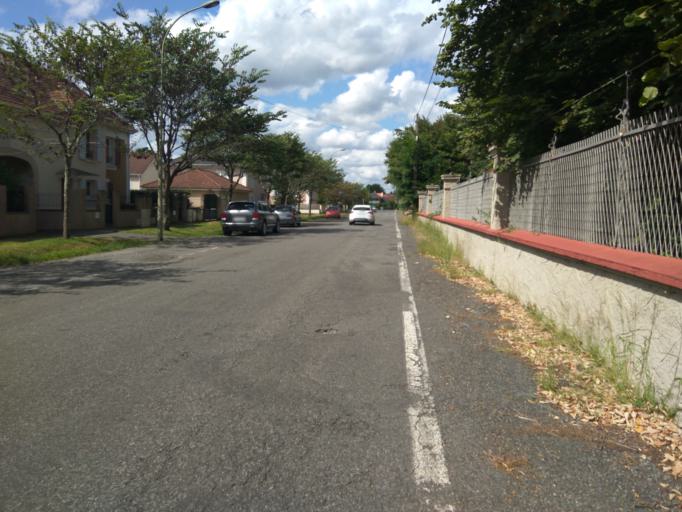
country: FR
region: Aquitaine
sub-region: Departement des Pyrenees-Atlantiques
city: Bizanos
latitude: 43.2997
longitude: -0.3389
